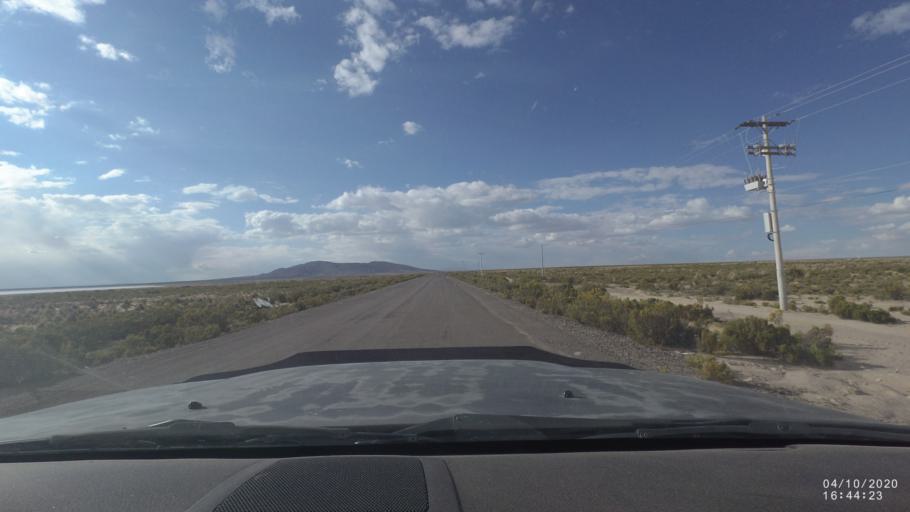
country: BO
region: Oruro
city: Poopo
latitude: -18.6846
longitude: -67.5591
